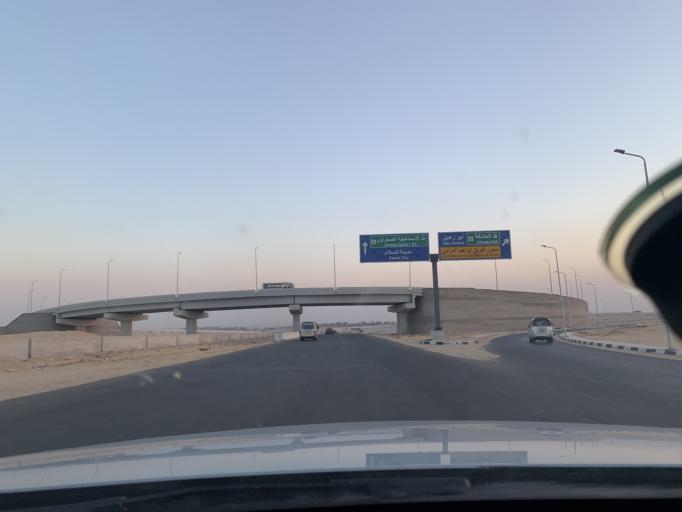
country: EG
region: Muhafazat al Qalyubiyah
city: Al Khankah
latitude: 30.2141
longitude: 31.4232
